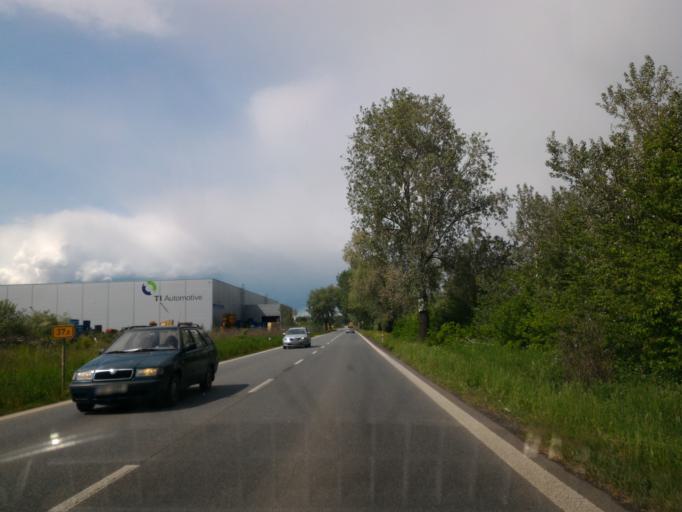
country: CZ
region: Central Bohemia
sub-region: Okres Mlada Boleslav
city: Mlada Boleslav
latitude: 50.3751
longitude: 14.9008
